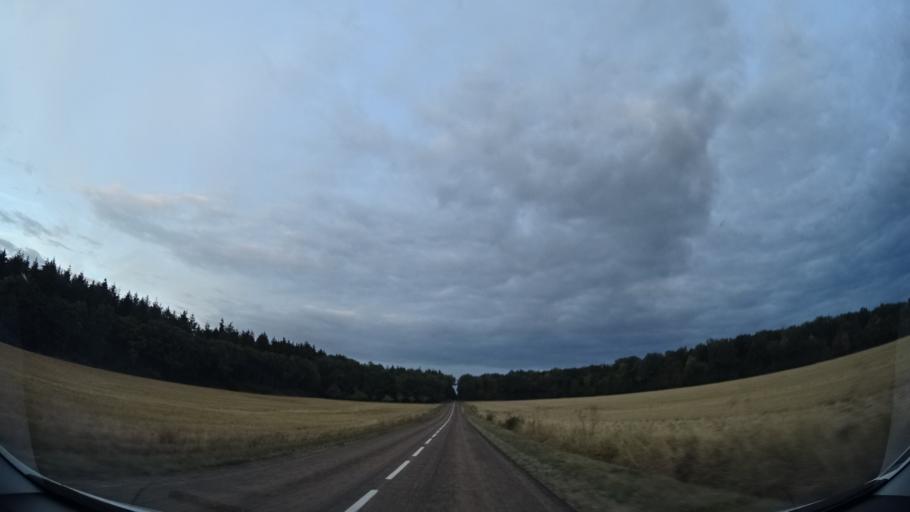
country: FR
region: Bourgogne
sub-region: Departement de l'Yonne
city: Cezy
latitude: 47.9292
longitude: 3.2764
